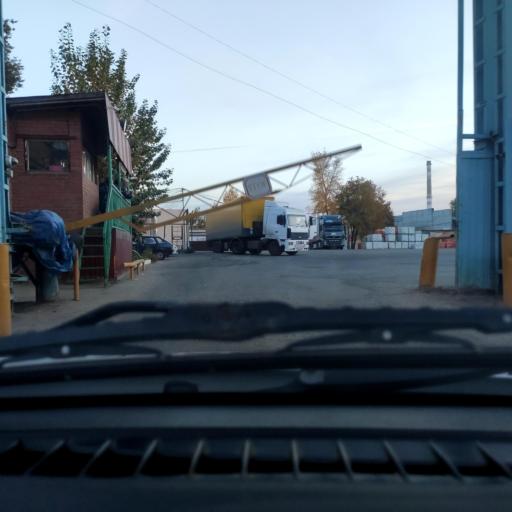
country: RU
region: Samara
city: Zhigulevsk
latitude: 53.4816
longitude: 49.4875
